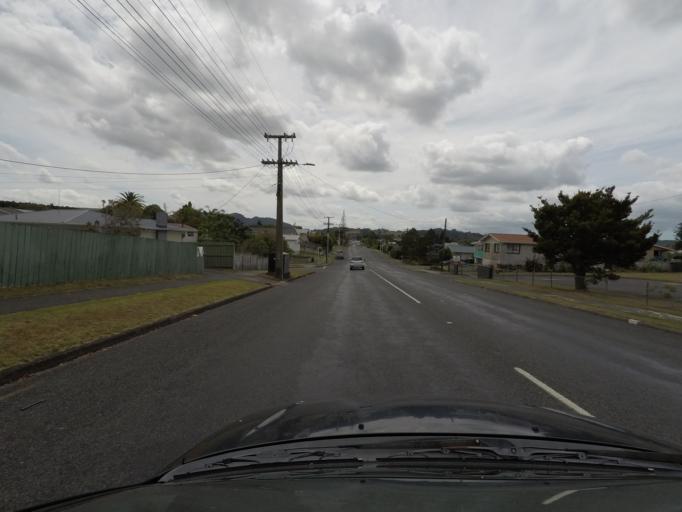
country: NZ
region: Northland
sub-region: Whangarei
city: Whangarei
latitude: -35.6840
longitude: 174.3277
